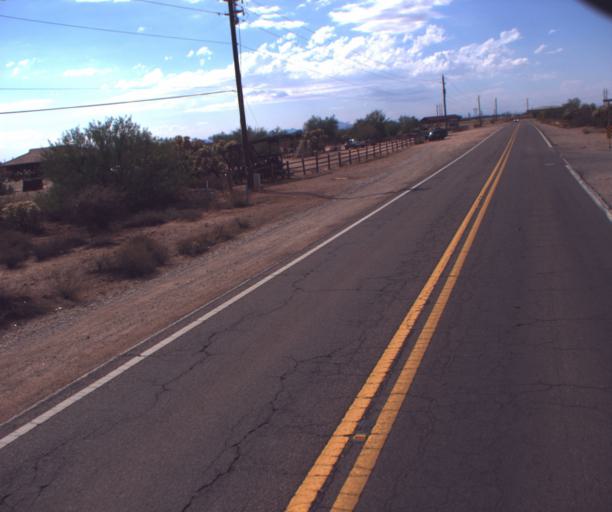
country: US
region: Arizona
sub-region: Pinal County
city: Apache Junction
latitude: 33.4481
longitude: -111.5016
